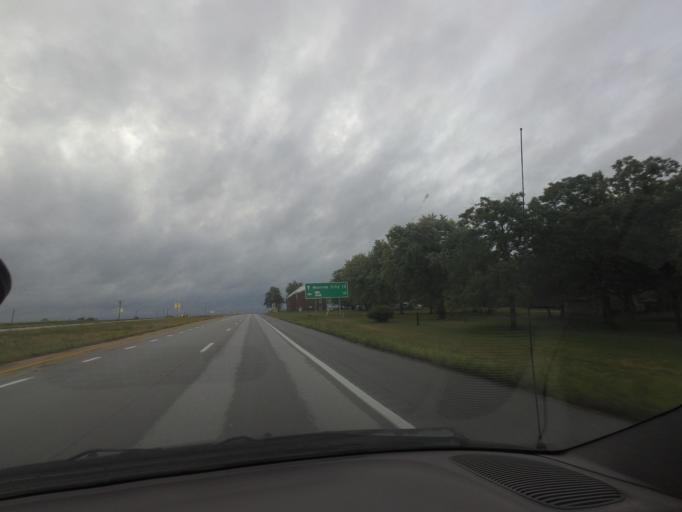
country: US
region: Missouri
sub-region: Shelby County
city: Shelbina
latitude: 39.6745
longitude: -91.9522
